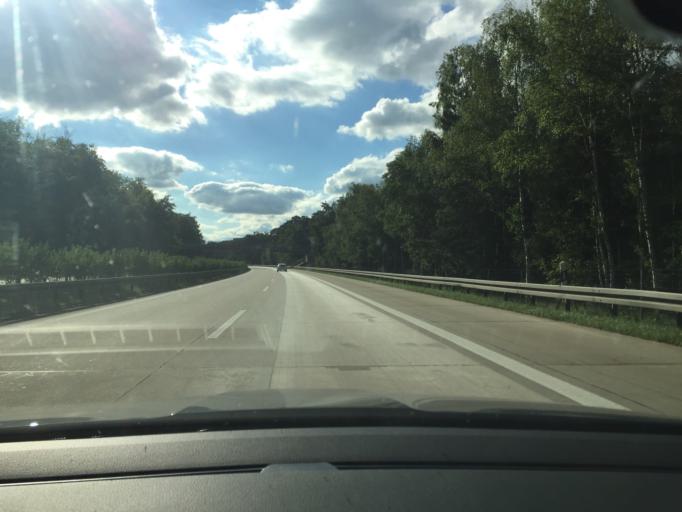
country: DE
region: Brandenburg
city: Berkenbruck
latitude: 52.3414
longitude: 14.1953
